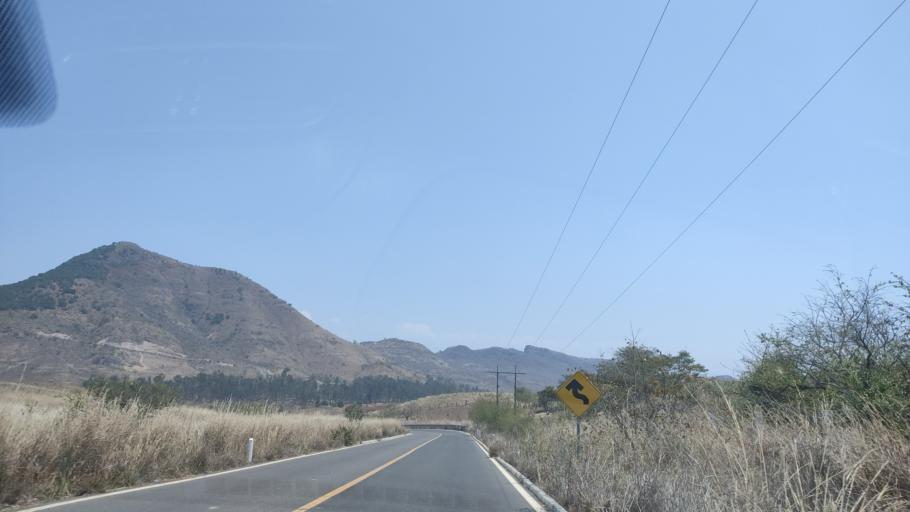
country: MX
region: Nayarit
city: Puga
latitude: 21.6100
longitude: -104.7284
